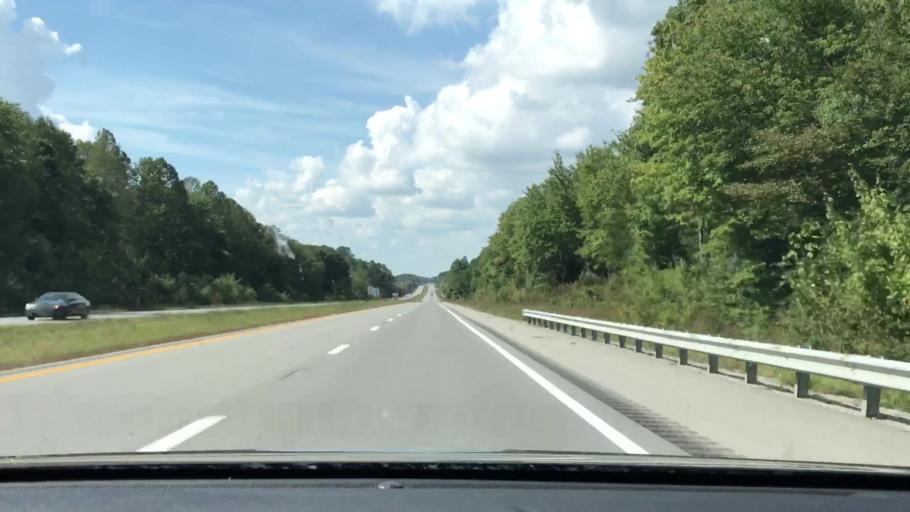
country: US
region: Kentucky
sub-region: Russell County
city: Russell Springs
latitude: 37.0451
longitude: -85.1083
